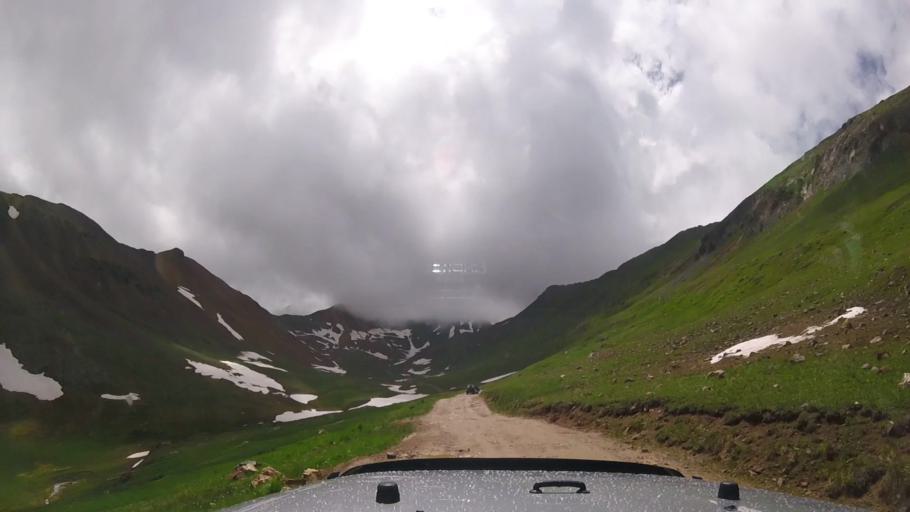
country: US
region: Colorado
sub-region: Ouray County
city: Ouray
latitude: 37.9256
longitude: -107.6099
